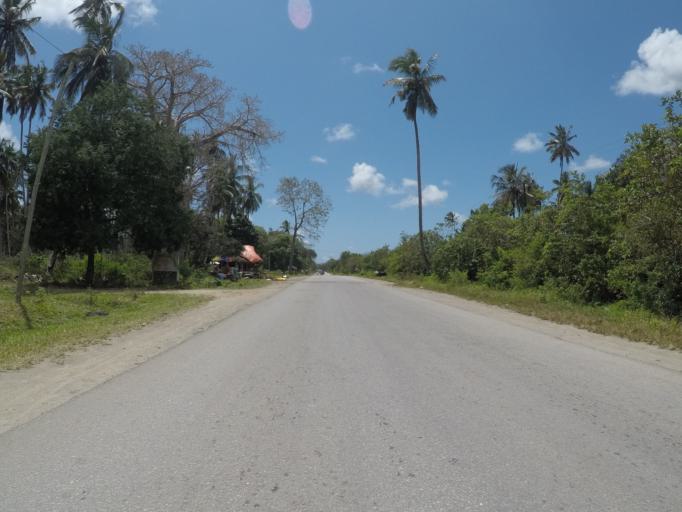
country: TZ
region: Zanzibar Central/South
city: Nganane
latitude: -6.2722
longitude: 39.4200
